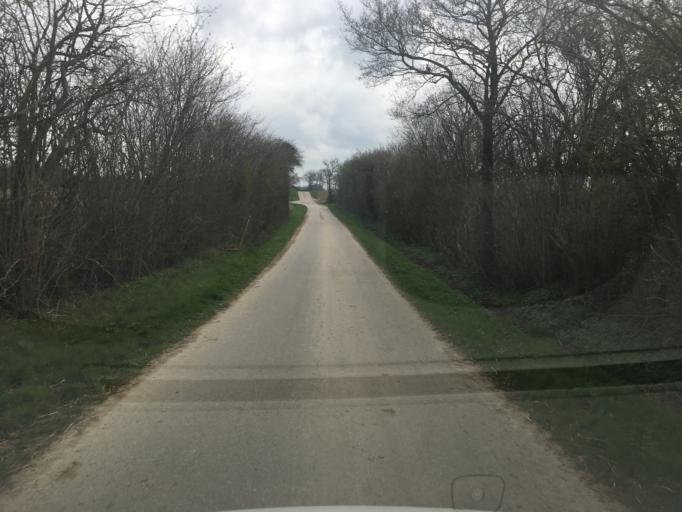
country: DE
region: Schleswig-Holstein
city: Glucksburg
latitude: 54.8971
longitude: 9.4988
